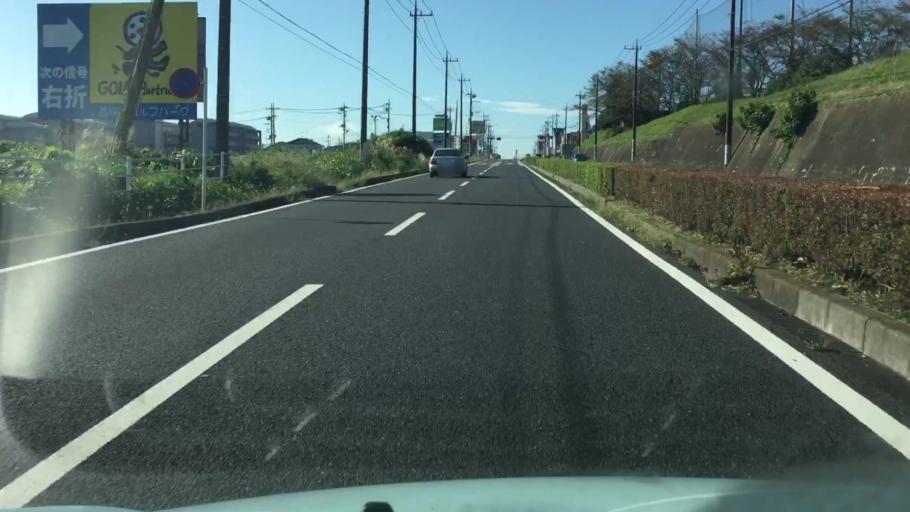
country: JP
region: Tochigi
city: Ujiie
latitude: 36.6260
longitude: 139.9928
